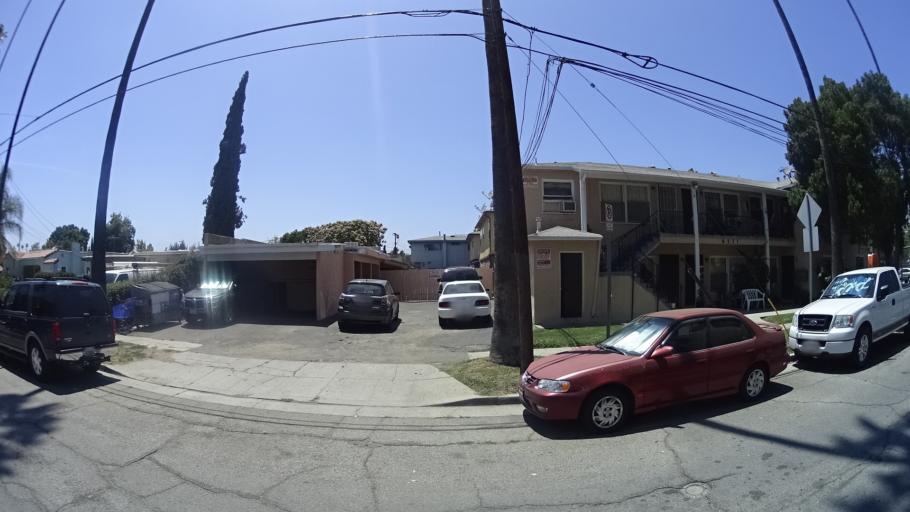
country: US
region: California
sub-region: Los Angeles County
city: Van Nuys
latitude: 34.1936
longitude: -118.4445
